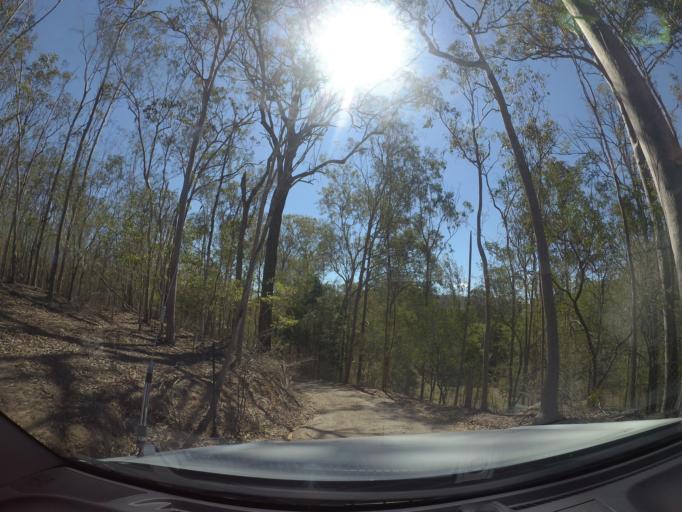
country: AU
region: Queensland
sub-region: Ipswich
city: Springfield Lakes
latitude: -27.7546
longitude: 152.8820
